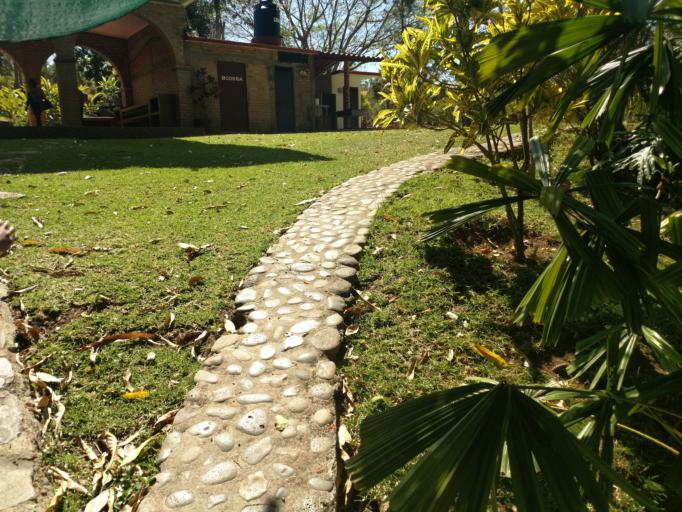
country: MX
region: Nayarit
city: Tepic
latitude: 21.5685
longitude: -104.9983
